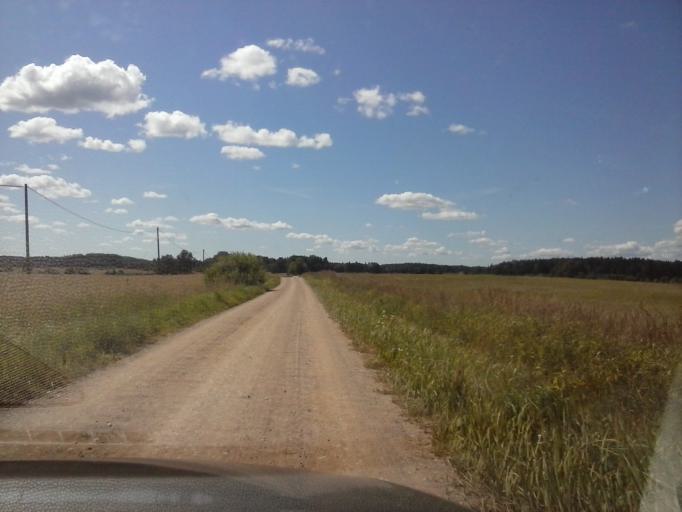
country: LV
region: Apes Novads
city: Ape
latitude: 57.5723
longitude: 26.6881
